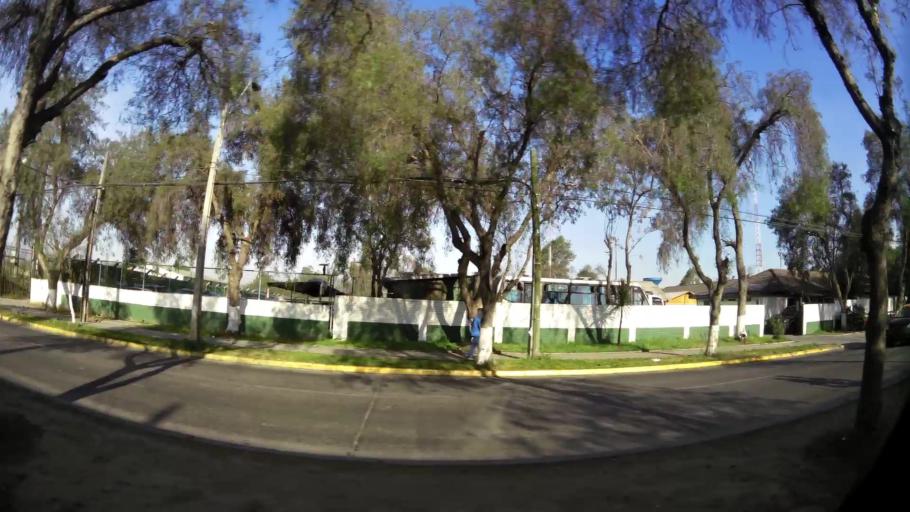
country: CL
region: Santiago Metropolitan
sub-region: Provincia de Santiago
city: Lo Prado
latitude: -33.4486
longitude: -70.7394
